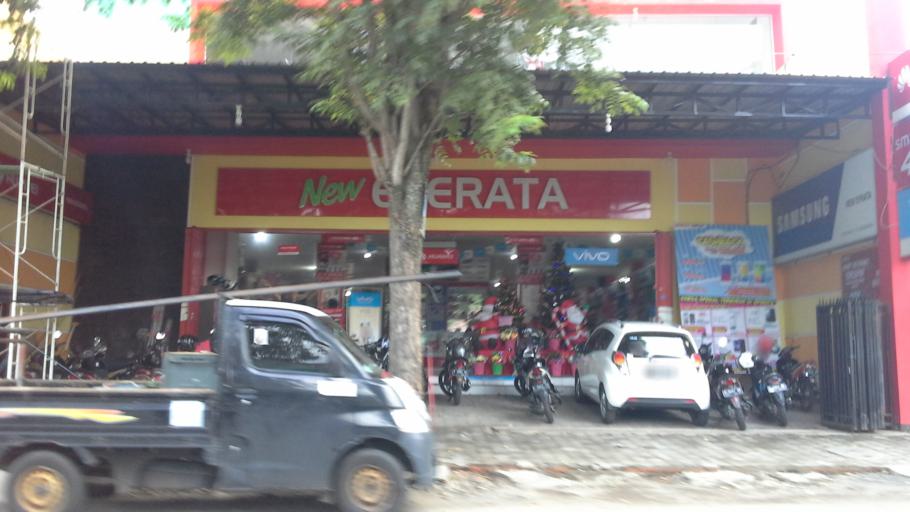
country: ID
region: East Java
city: Bondowoso
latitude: -7.9222
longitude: 113.8186
